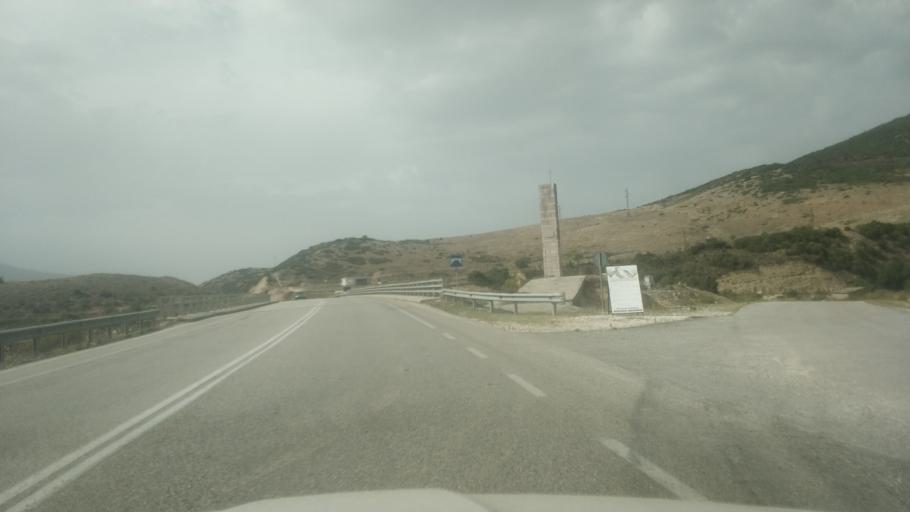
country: AL
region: Gjirokaster
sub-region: Rrethi i Tepelenes
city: Memaliaj
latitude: 40.3631
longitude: 19.9258
